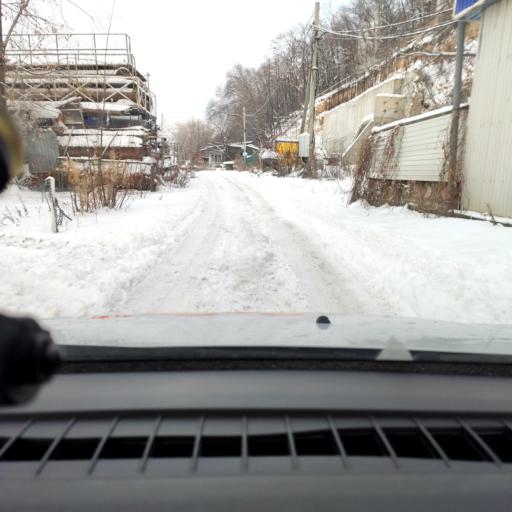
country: RU
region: Samara
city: Samara
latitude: 53.2862
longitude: 50.1907
